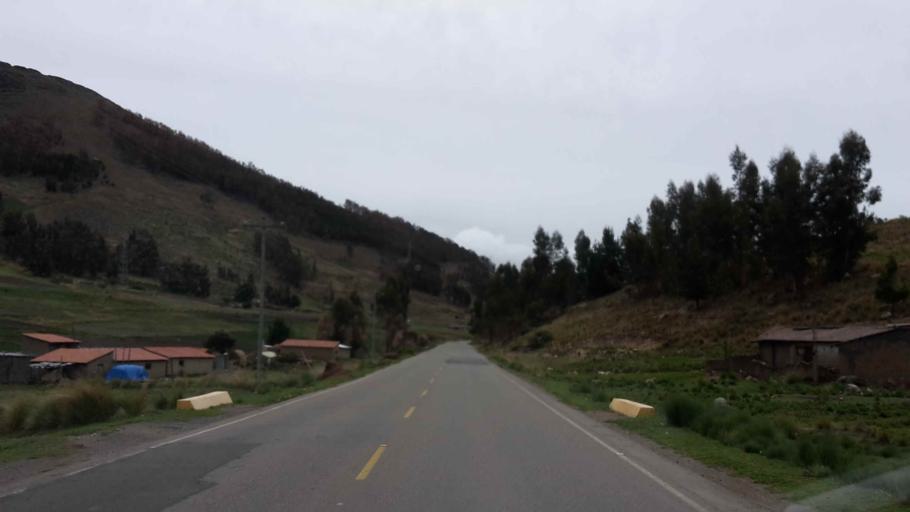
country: BO
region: Cochabamba
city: Arani
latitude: -17.4809
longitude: -65.5826
